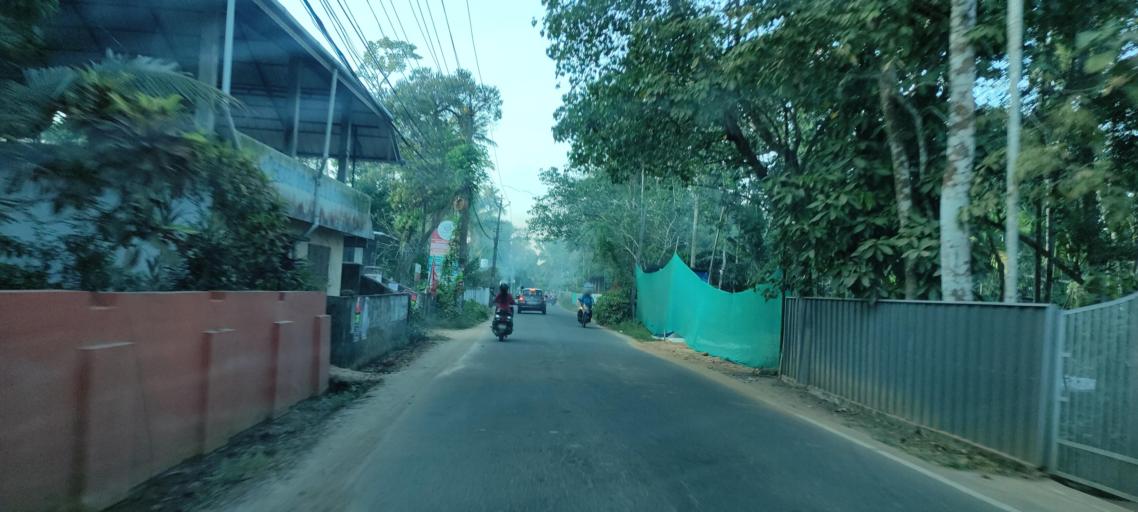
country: IN
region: Kerala
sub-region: Alappuzha
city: Kayankulam
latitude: 9.2466
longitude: 76.4525
